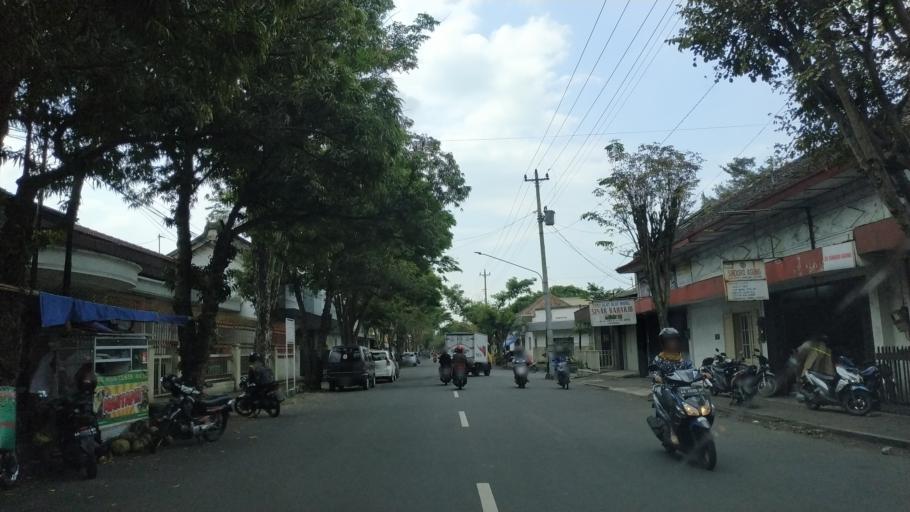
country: ID
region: Central Java
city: Magelang
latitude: -7.3153
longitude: 110.1772
